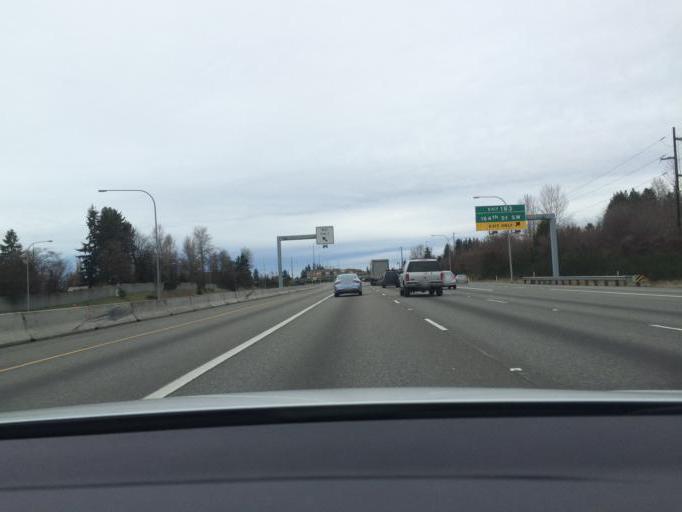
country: US
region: Washington
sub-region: Snohomish County
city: Martha Lake
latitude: 47.8444
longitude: -122.2587
